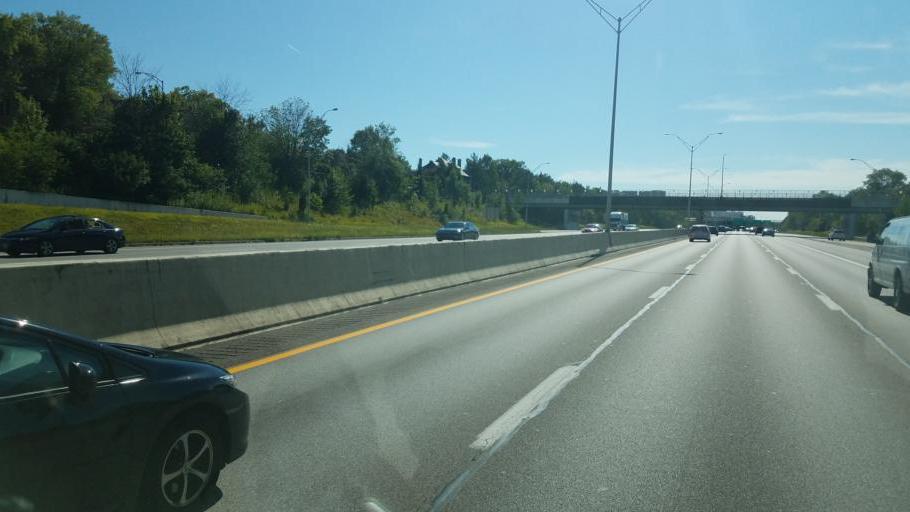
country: US
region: Ohio
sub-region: Franklin County
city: Bexley
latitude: 39.9537
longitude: -82.9636
